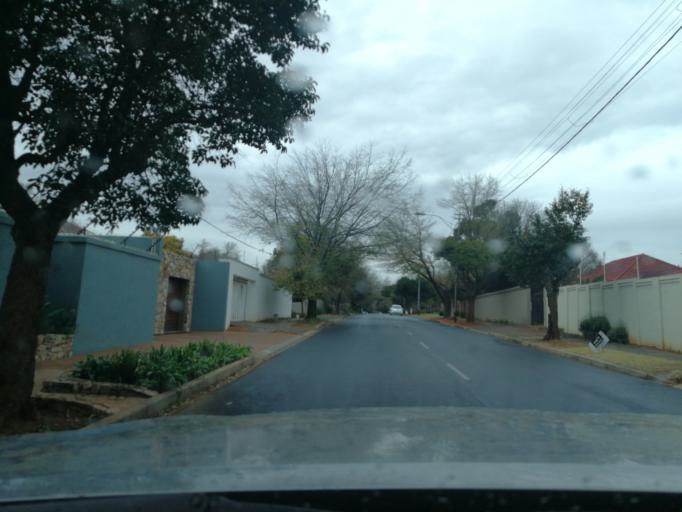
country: ZA
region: Gauteng
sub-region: City of Johannesburg Metropolitan Municipality
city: Johannesburg
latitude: -26.1506
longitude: 28.0160
